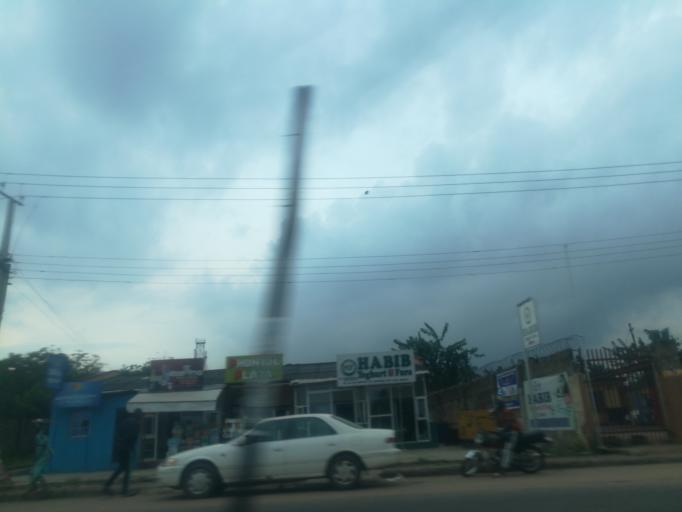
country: NG
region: Oyo
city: Ibadan
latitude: 7.4362
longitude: 3.9075
